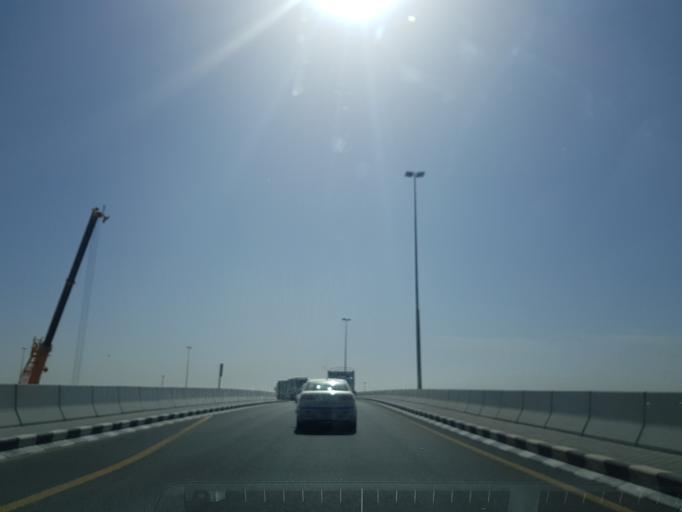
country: AE
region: Dubai
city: Dubai
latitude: 25.0136
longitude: 55.0909
